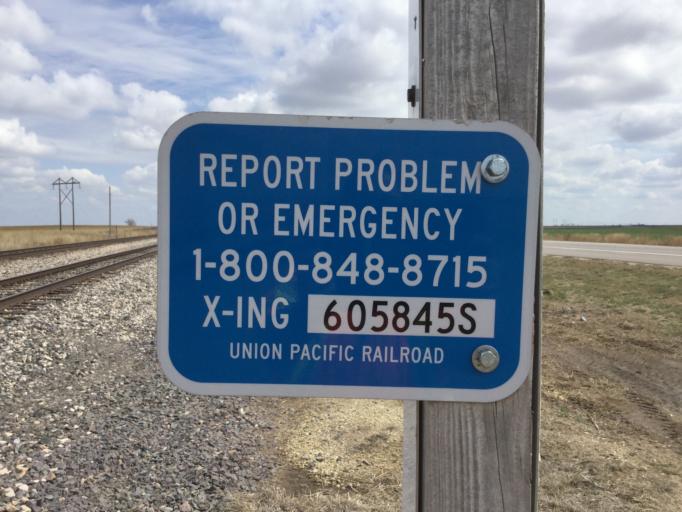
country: US
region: Kansas
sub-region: Kiowa County
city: Greensburg
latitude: 37.5985
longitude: -99.3761
